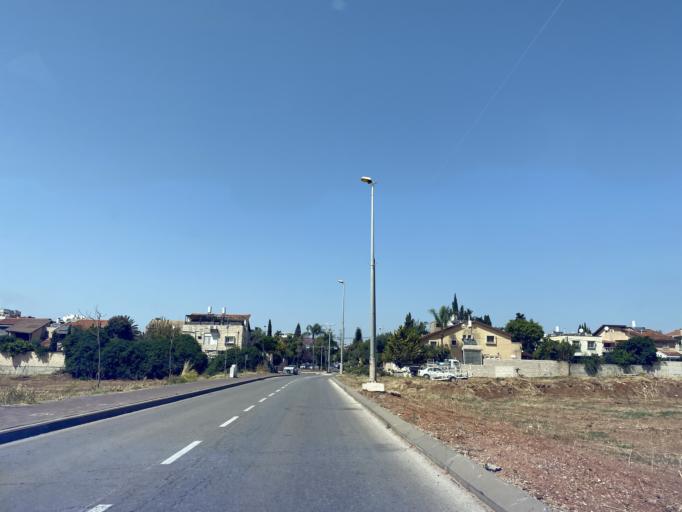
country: IL
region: Central District
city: Ra'anana
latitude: 32.1734
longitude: 34.8795
